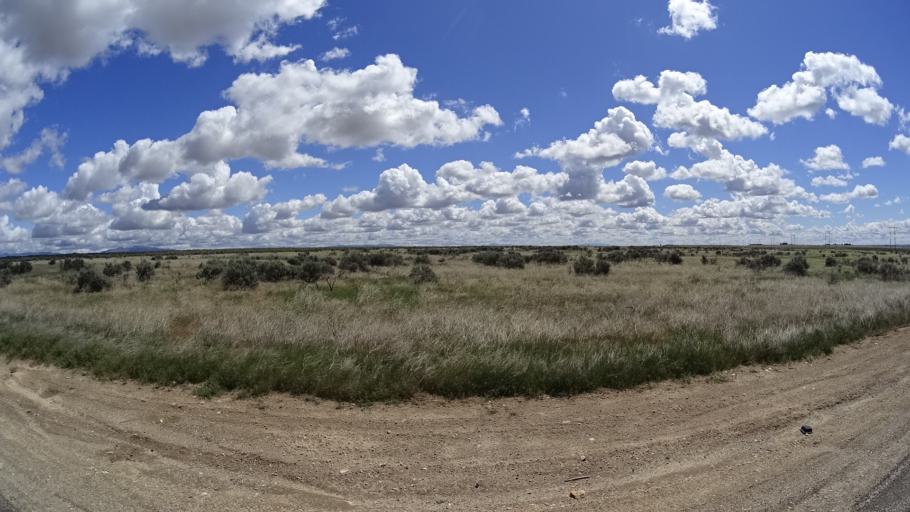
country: US
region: Idaho
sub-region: Ada County
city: Kuna
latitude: 43.4789
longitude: -116.2743
